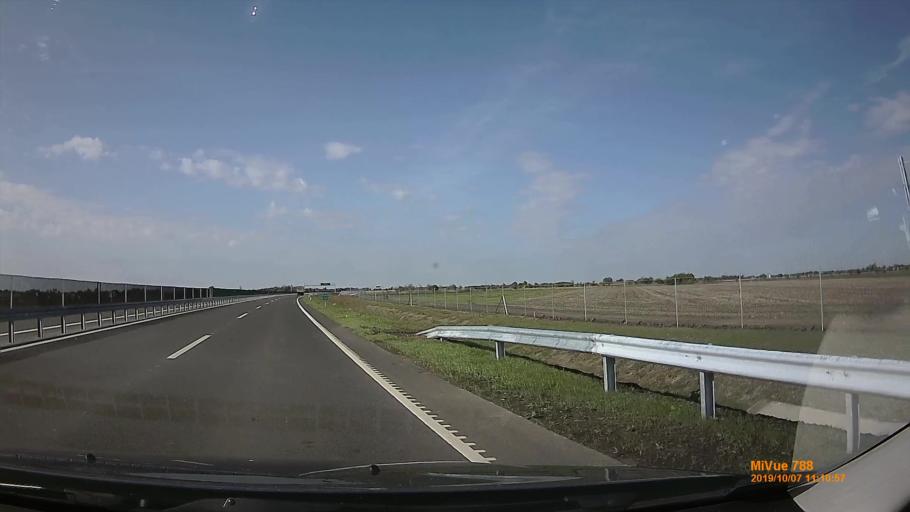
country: HU
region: Bekes
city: Kondoros
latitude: 46.7378
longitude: 20.8083
